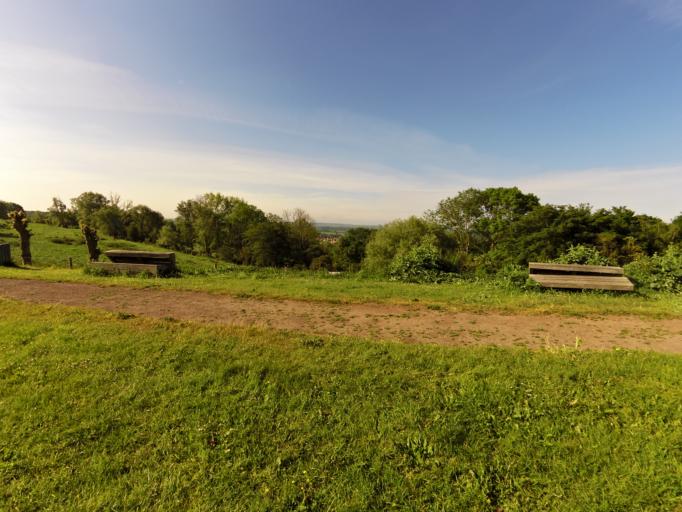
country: FR
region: Nord-Pas-de-Calais
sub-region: Departement du Nord
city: Watten
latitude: 50.8283
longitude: 2.2182
